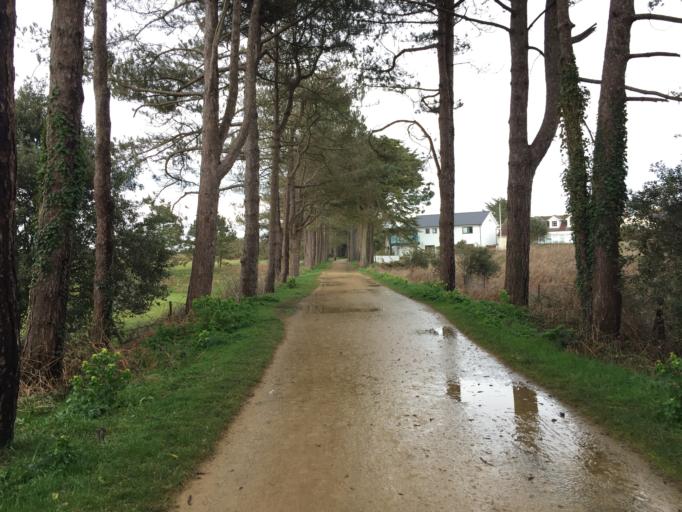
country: JE
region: St Helier
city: Saint Helier
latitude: 49.1907
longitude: -2.2140
